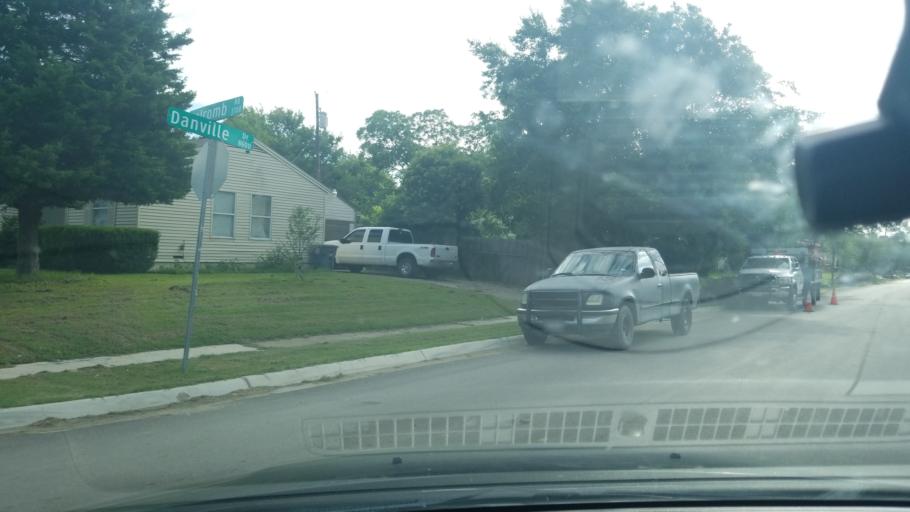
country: US
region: Texas
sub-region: Dallas County
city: Balch Springs
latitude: 32.7405
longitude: -96.6742
